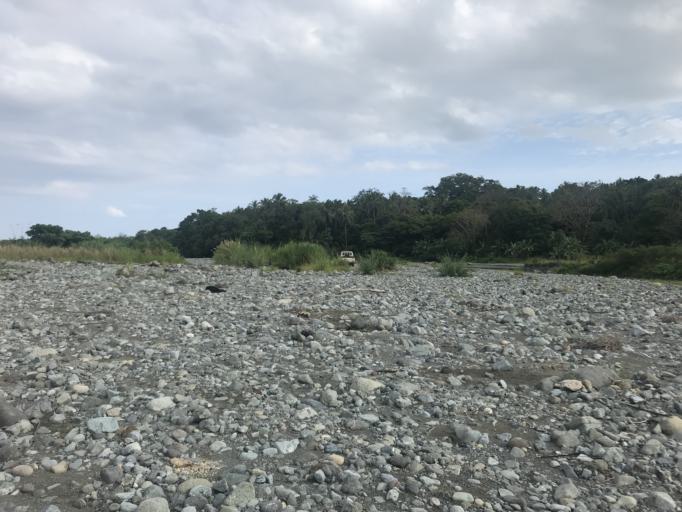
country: VU
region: Sanma
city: Luganville
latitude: -15.6111
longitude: 166.8694
